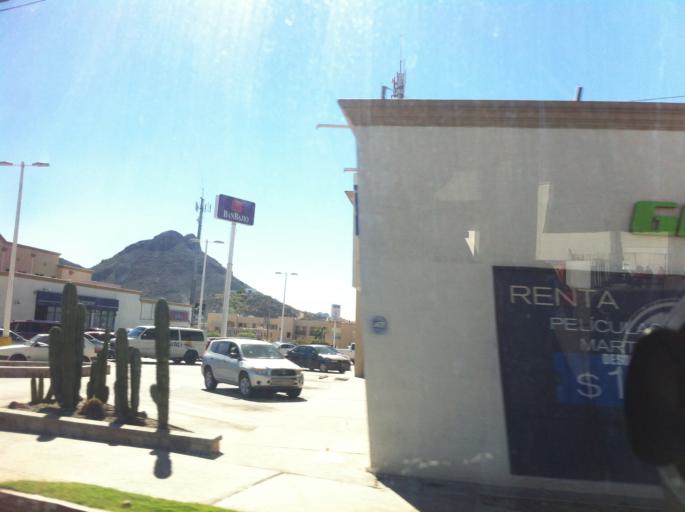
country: MX
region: Sonora
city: Heroica Guaymas
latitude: 27.9262
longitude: -110.9204
